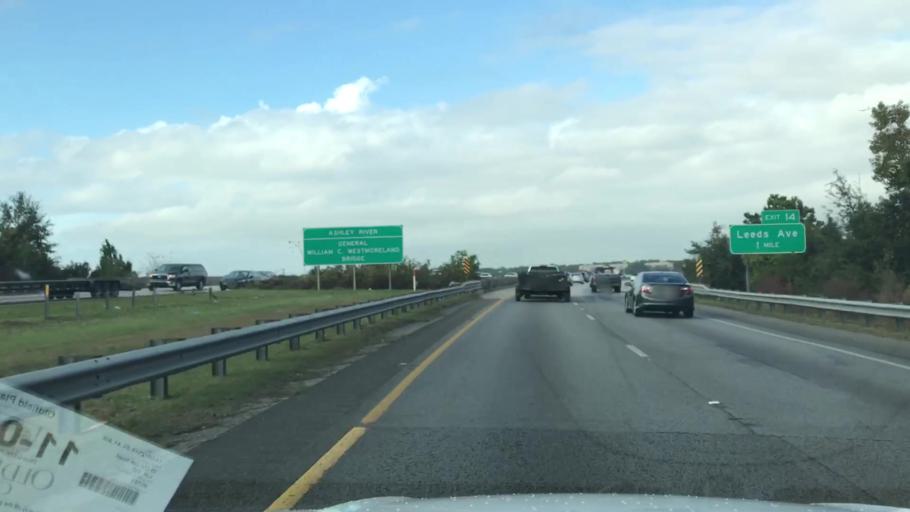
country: US
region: South Carolina
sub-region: Charleston County
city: North Charleston
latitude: 32.8282
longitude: -80.0296
